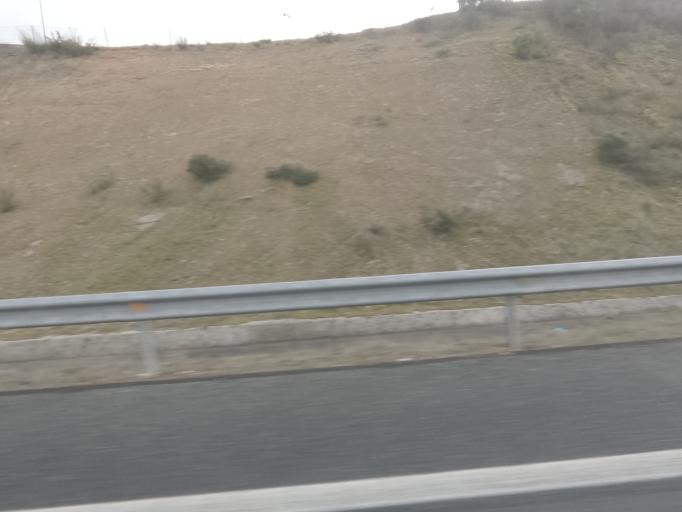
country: ES
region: Galicia
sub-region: Provincia de Pontevedra
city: Lalin
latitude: 42.6731
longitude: -8.1597
